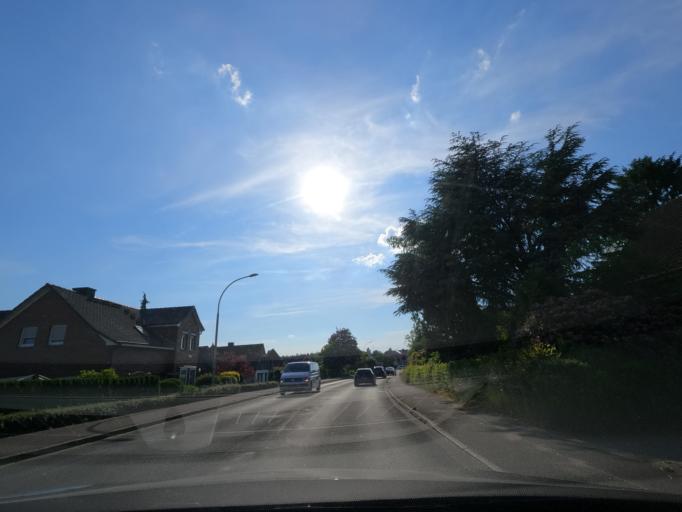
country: DE
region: Schleswig-Holstein
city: Appen
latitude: 53.6593
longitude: 9.7523
